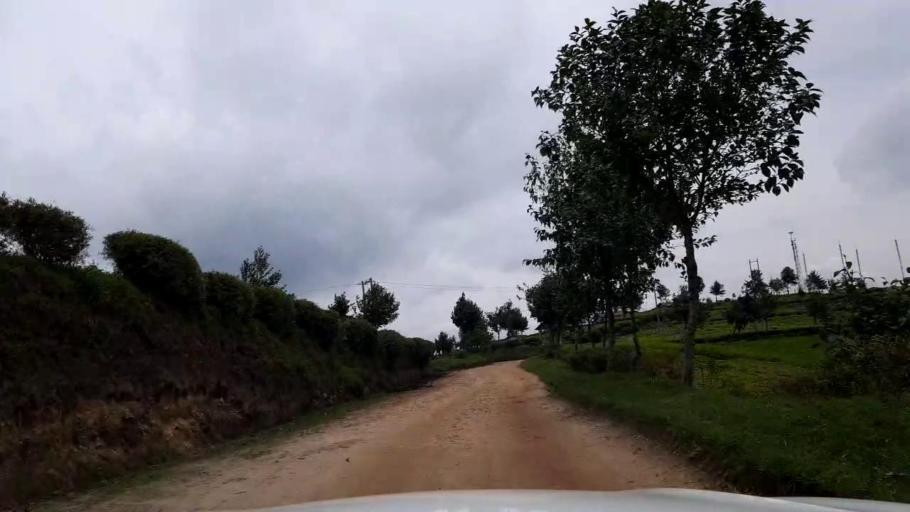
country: RW
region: Western Province
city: Kibuye
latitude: -1.9531
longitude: 29.4130
